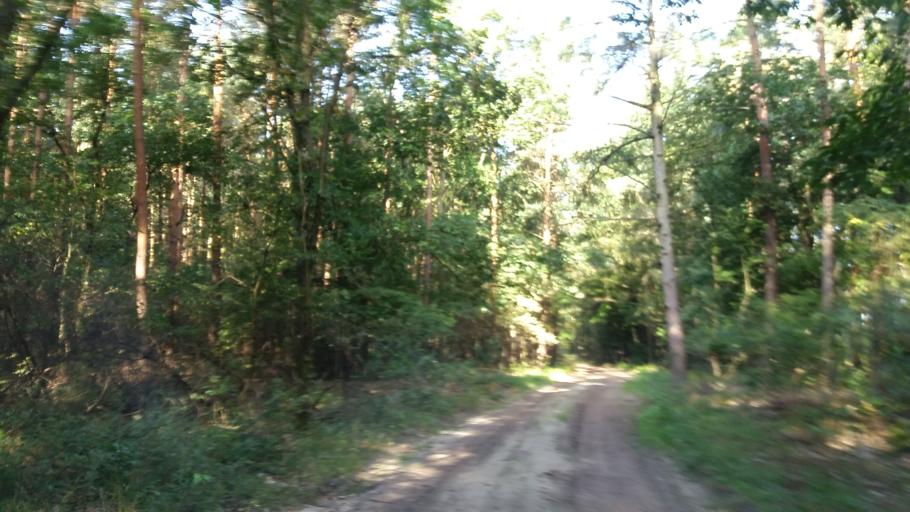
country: PL
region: West Pomeranian Voivodeship
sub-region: Powiat choszczenski
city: Choszczno
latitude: 53.2414
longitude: 15.4163
